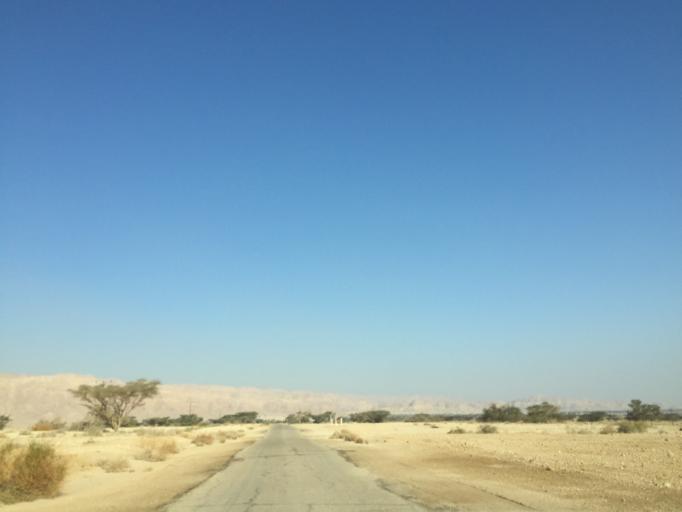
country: JO
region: Ma'an
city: Al Quwayrah
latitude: 29.8370
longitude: 35.0314
